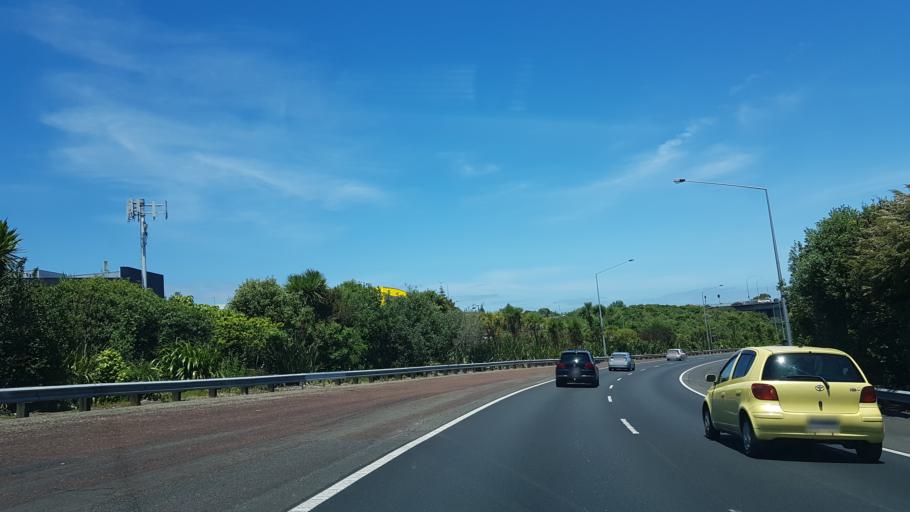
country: NZ
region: Auckland
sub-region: Auckland
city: Auckland
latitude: -36.8605
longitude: 174.7565
